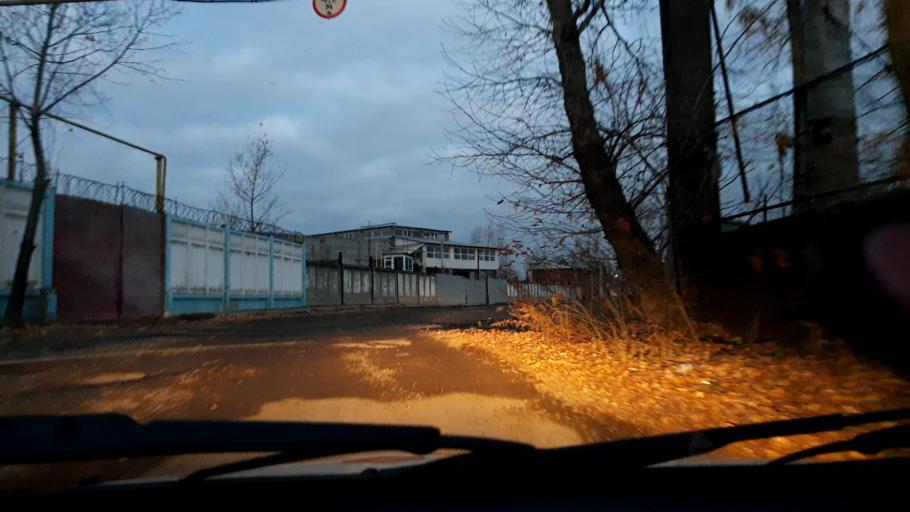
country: RU
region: Bashkortostan
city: Ufa
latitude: 54.8335
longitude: 56.1172
